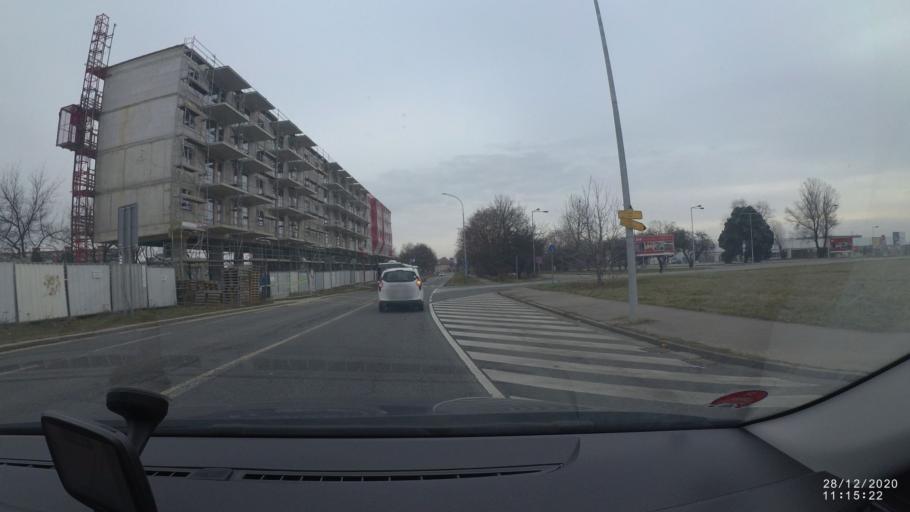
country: CZ
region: Praha
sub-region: Praha 18
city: Letnany
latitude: 50.1291
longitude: 14.5113
